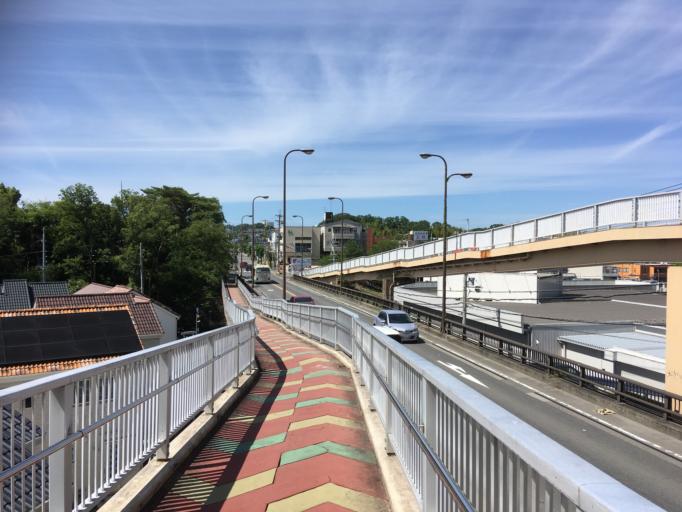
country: JP
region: Nara
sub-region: Ikoma-shi
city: Ikoma
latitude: 34.7062
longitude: 135.7502
